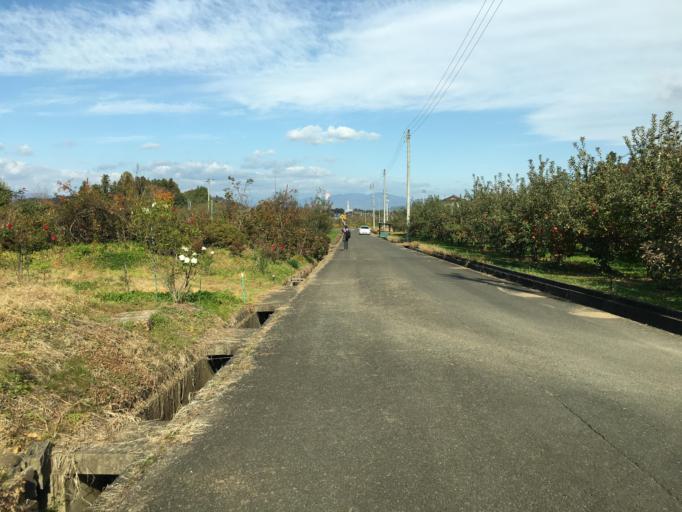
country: JP
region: Fukushima
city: Fukushima-shi
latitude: 37.7035
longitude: 140.4356
